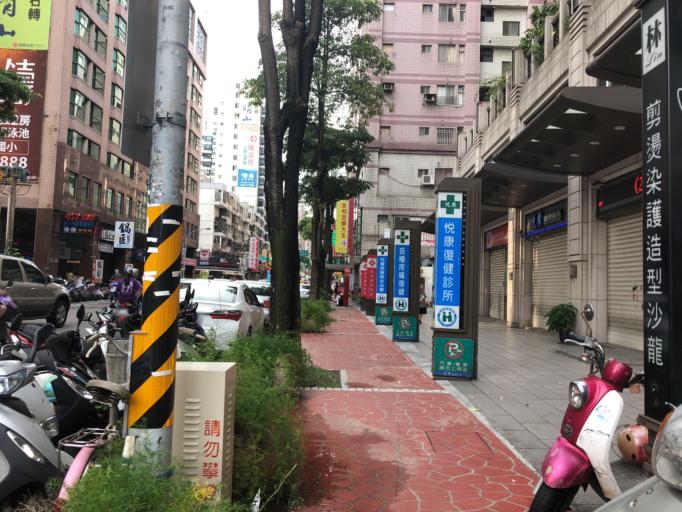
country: TW
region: Taiwan
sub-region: Taoyuan
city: Taoyuan
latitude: 25.0123
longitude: 121.3185
